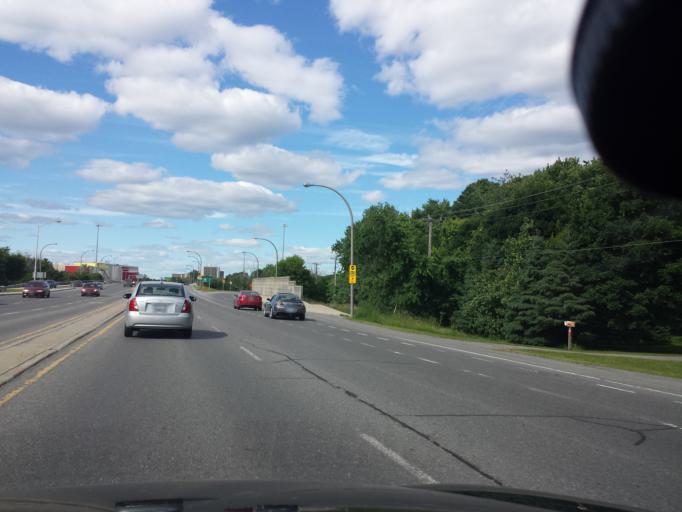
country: CA
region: Ontario
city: Bells Corners
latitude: 45.3431
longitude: -75.8072
